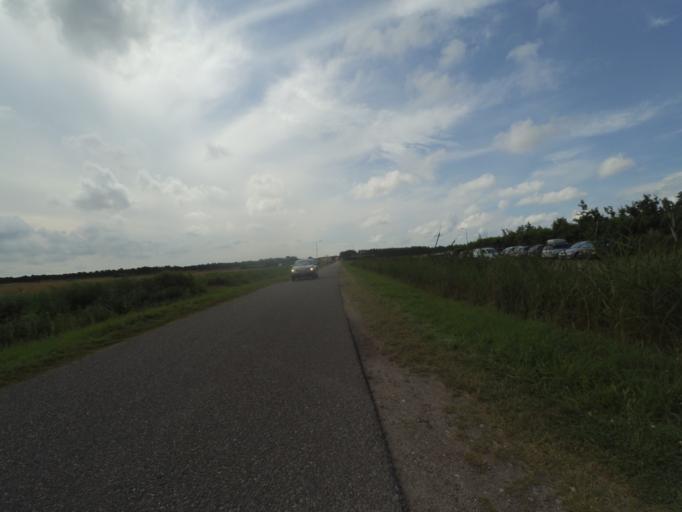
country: NL
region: North Holland
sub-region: Gemeente Texel
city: Den Burg
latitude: 53.0249
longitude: 4.7422
